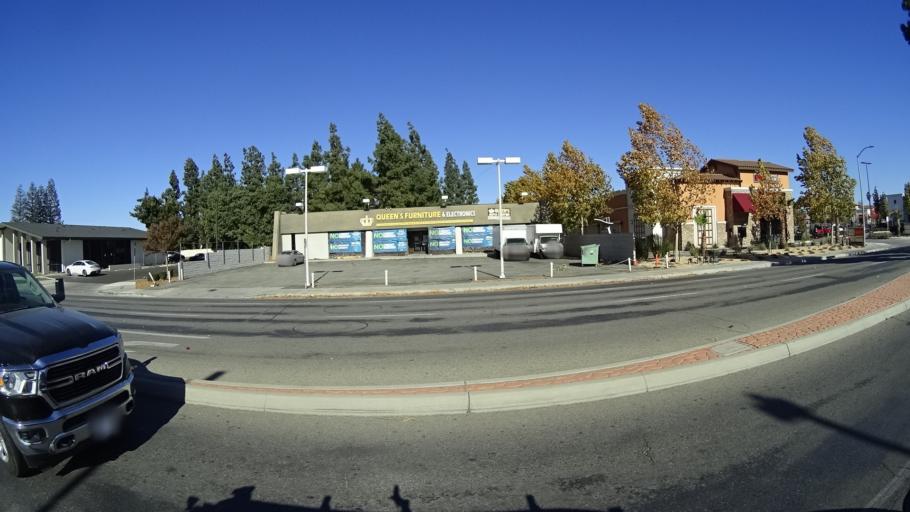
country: US
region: California
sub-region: Kern County
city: Bakersfield
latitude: 35.3673
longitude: -119.0468
